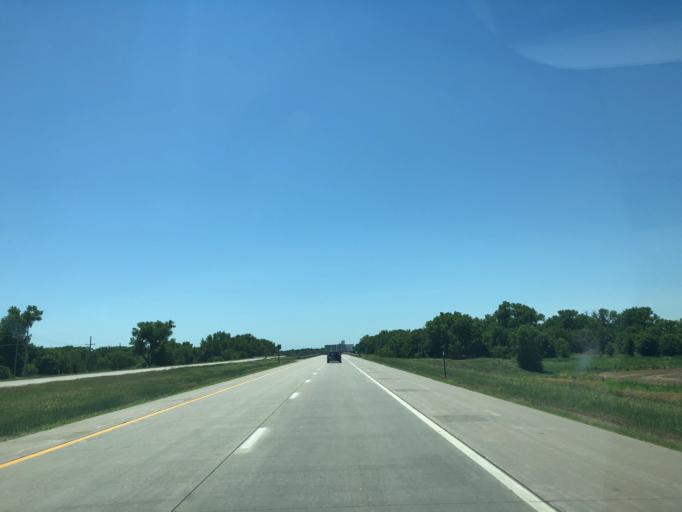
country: US
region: Kansas
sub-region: Cloud County
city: Concordia
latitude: 39.5939
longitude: -97.6594
